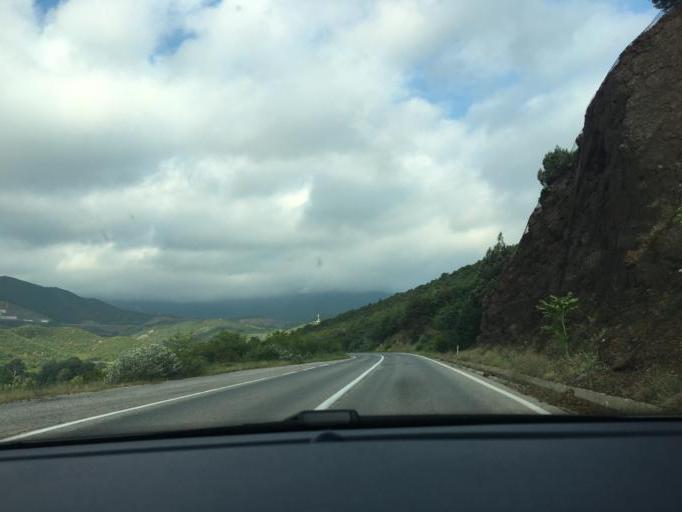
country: MK
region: Demir Kapija
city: Demir Kapija
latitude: 41.3931
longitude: 22.3306
